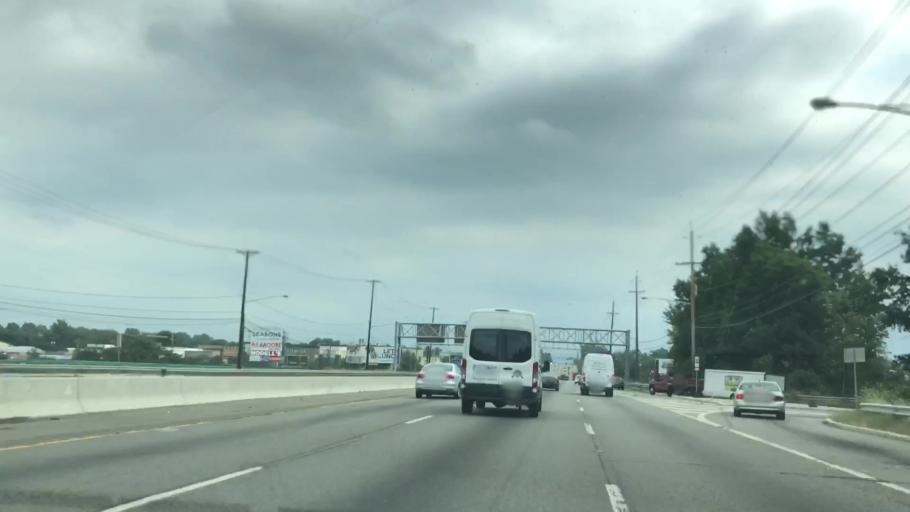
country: US
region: New Jersey
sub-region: Essex County
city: Nutley
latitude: 40.8400
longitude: -74.1606
